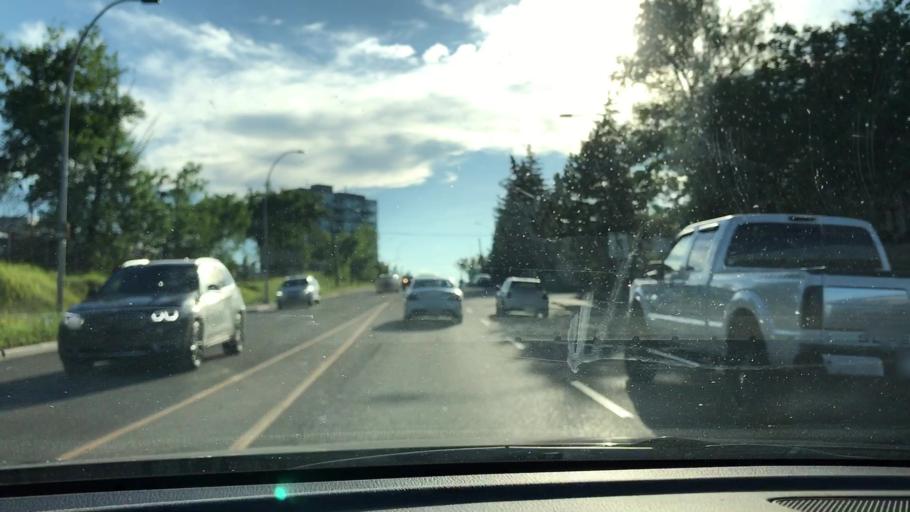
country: CA
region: Alberta
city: Calgary
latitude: 51.0379
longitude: -114.1145
